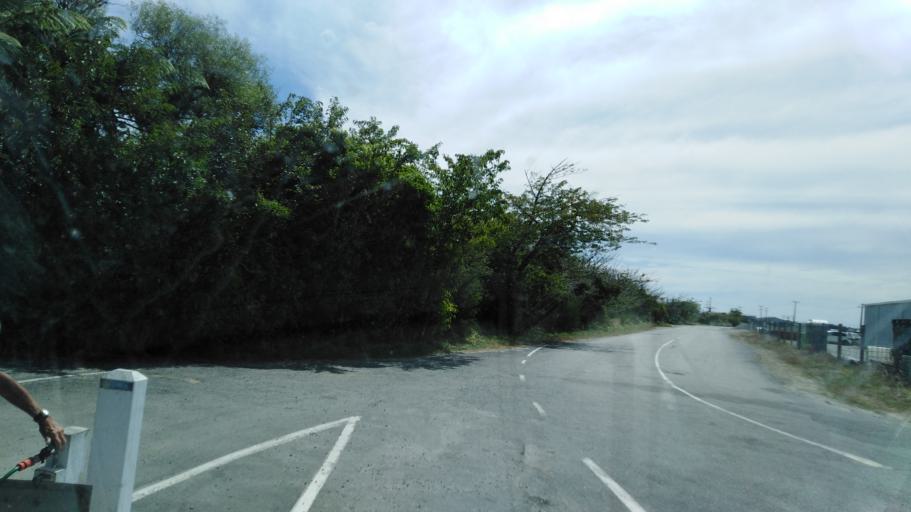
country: NZ
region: West Coast
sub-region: Buller District
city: Westport
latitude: -41.7587
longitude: 171.5972
